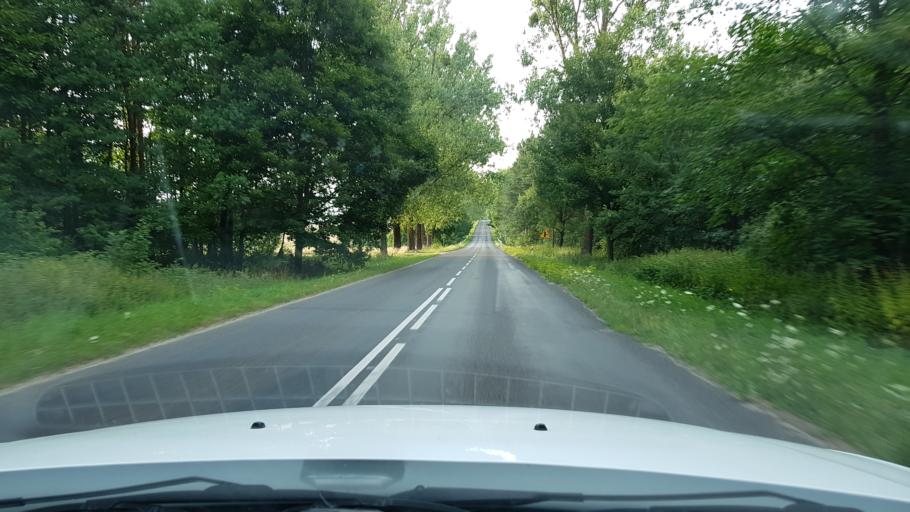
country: PL
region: West Pomeranian Voivodeship
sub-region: Powiat swidwinski
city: Polczyn-Zdroj
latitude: 53.8271
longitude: 16.0783
